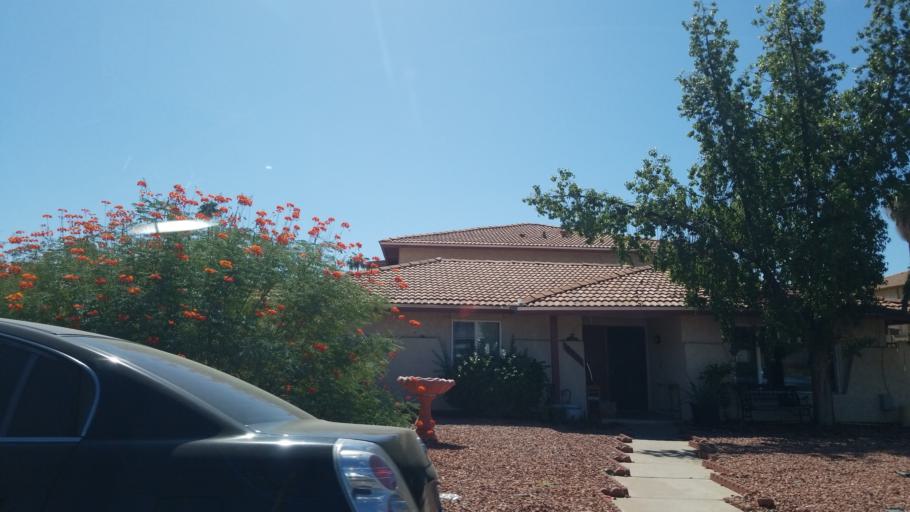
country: US
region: Arizona
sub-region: Maricopa County
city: Glendale
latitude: 33.5021
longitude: -112.1734
